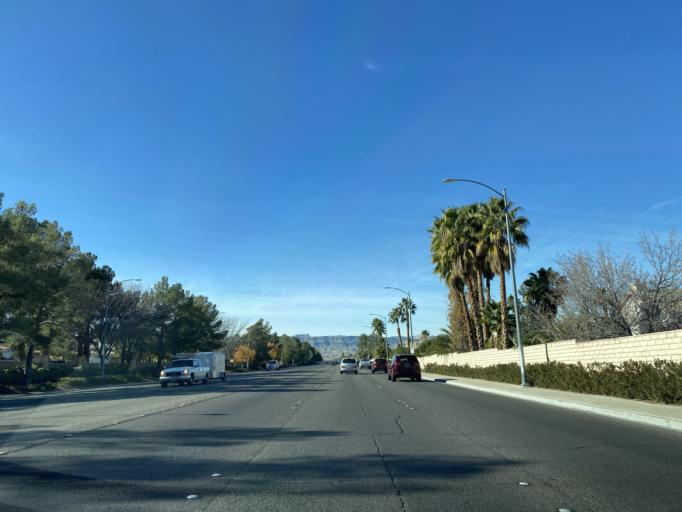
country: US
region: Nevada
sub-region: Clark County
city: Spring Valley
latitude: 36.1000
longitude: -115.2737
